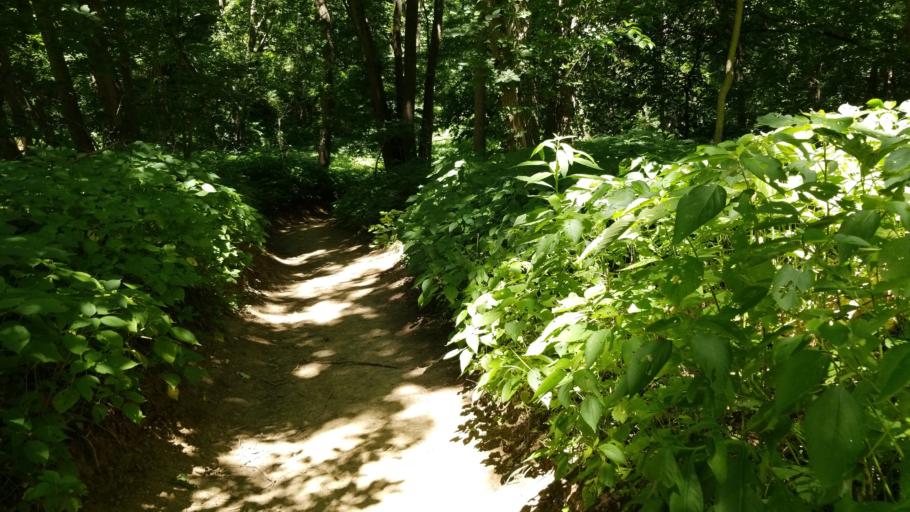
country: US
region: Iowa
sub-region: Pottawattamie County
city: Carter Lake
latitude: 41.3914
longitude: -95.9540
